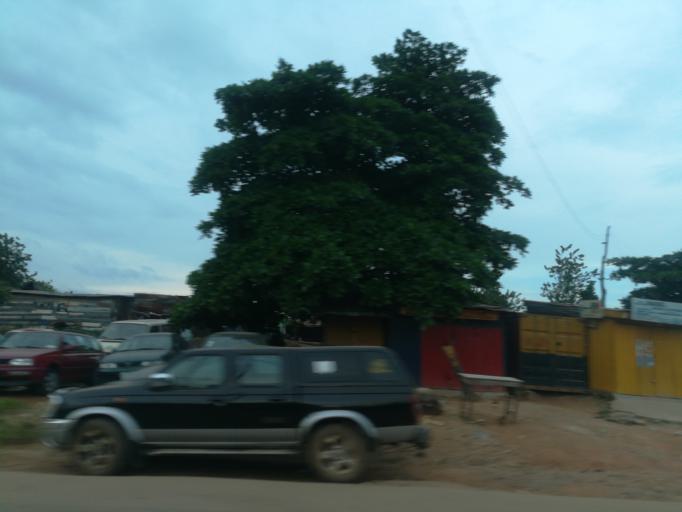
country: NG
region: Oyo
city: Ibadan
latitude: 7.4298
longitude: 3.9119
